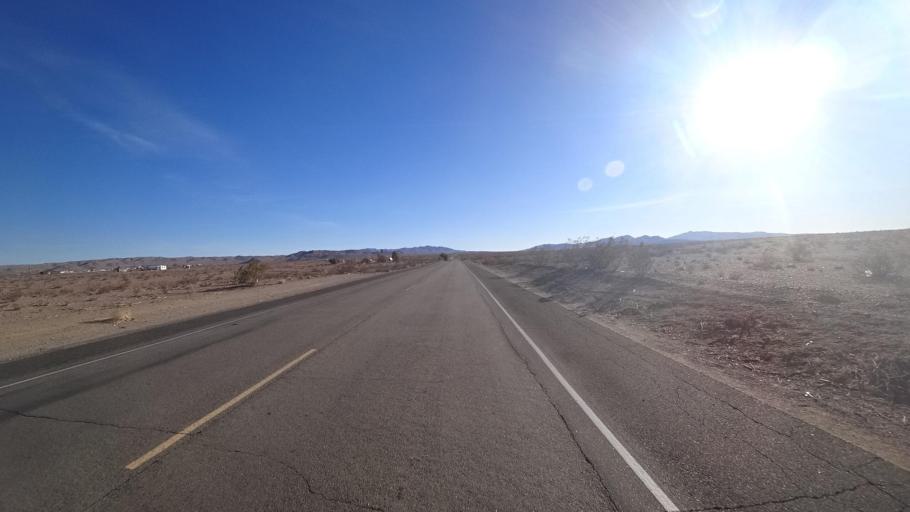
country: US
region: California
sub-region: Kern County
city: China Lake Acres
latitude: 35.6130
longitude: -117.7231
